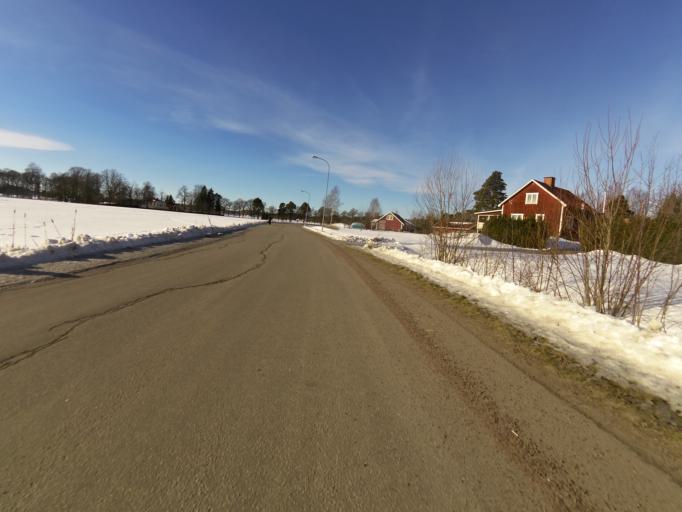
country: SE
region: Gaevleborg
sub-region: Gavle Kommun
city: Valbo
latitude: 60.6487
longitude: 17.0442
